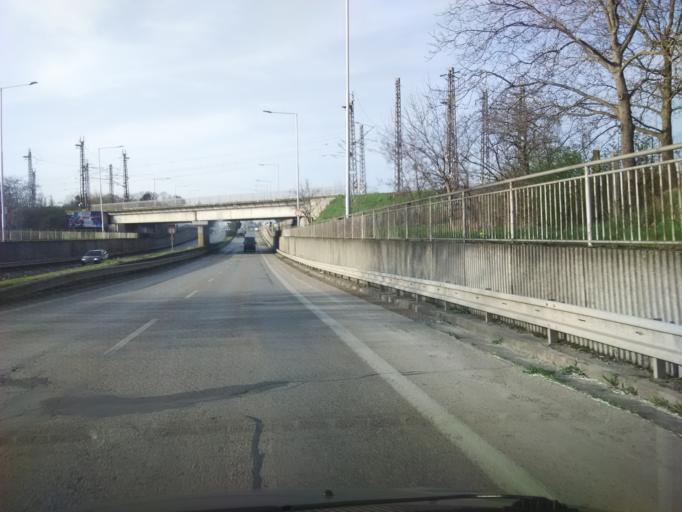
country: SK
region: Nitriansky
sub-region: Okres Nove Zamky
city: Nove Zamky
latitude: 48.0044
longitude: 18.1570
